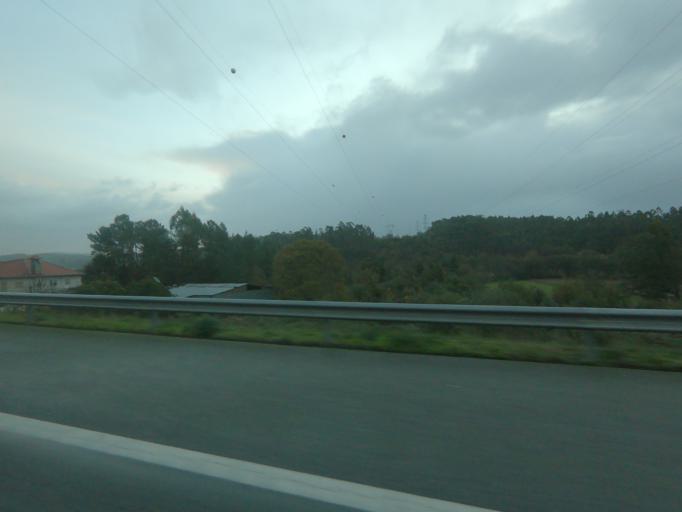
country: PT
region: Braga
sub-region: Barcelos
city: Galegos
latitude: 41.6375
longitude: -8.5598
